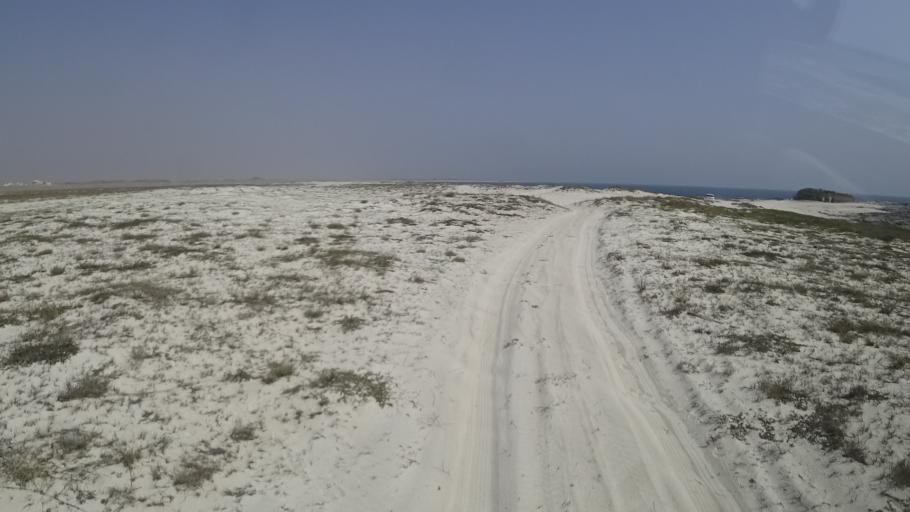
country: OM
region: Zufar
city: Salalah
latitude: 16.9697
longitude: 54.7048
